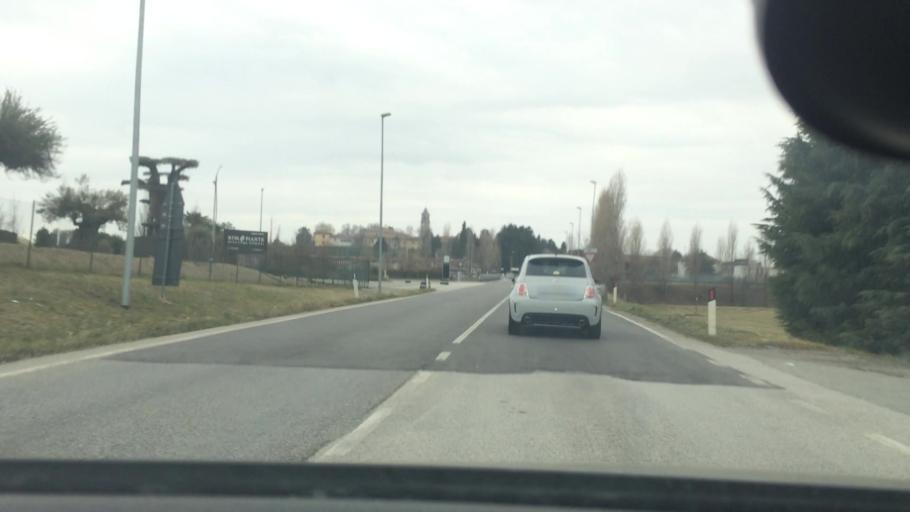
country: IT
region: Lombardy
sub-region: Provincia di Como
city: Lurago d'Erba
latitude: 45.7596
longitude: 9.2261
